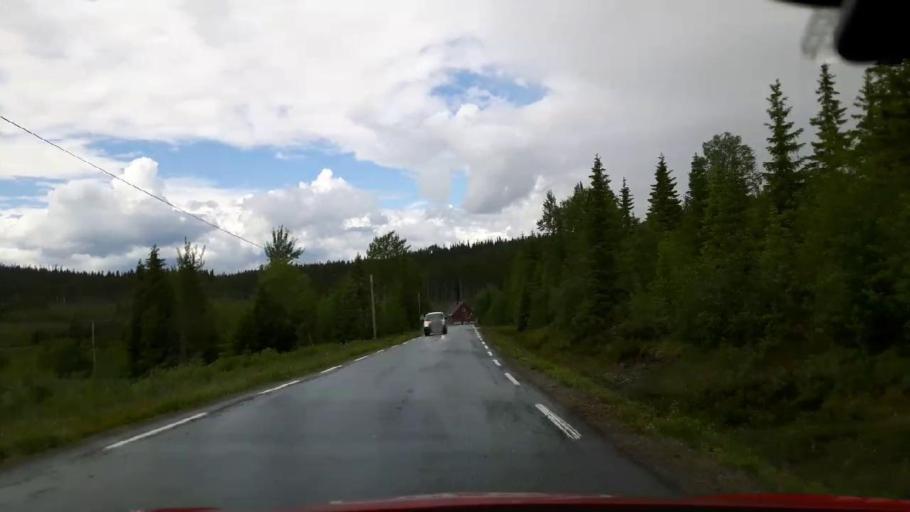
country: NO
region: Nord-Trondelag
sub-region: Lierne
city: Sandvika
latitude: 64.1004
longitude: 14.0247
